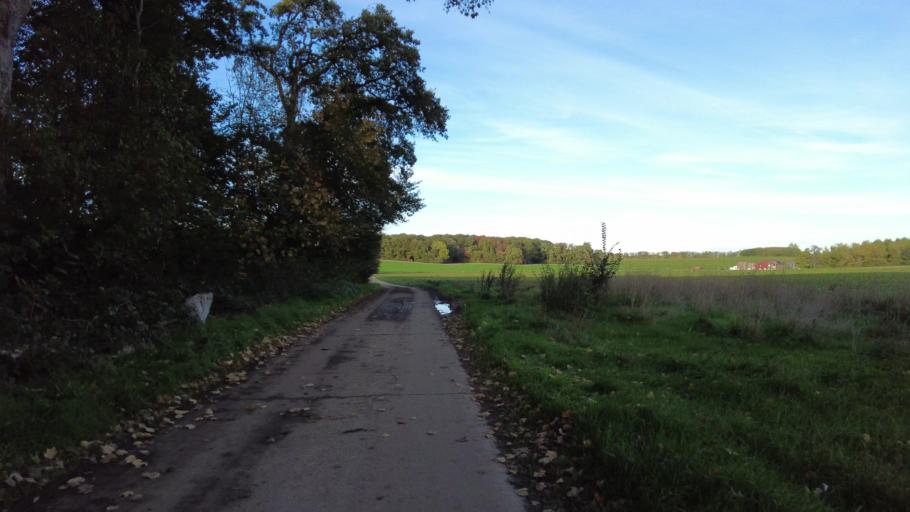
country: BE
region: Flanders
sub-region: Provincie Vlaams-Brabant
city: Hoegaarden
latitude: 50.7364
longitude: 4.9490
